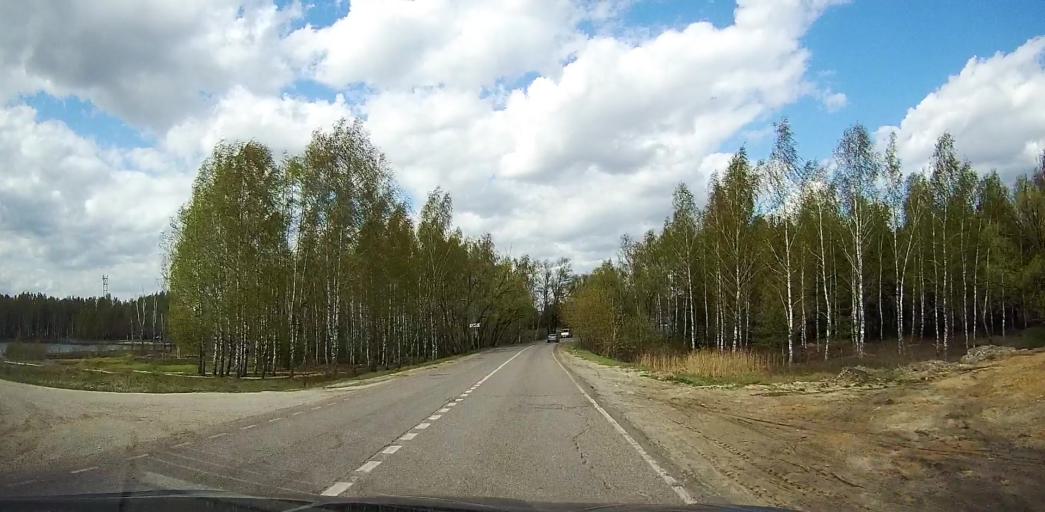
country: RU
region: Moskovskaya
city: Davydovo
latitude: 55.6067
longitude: 38.8478
